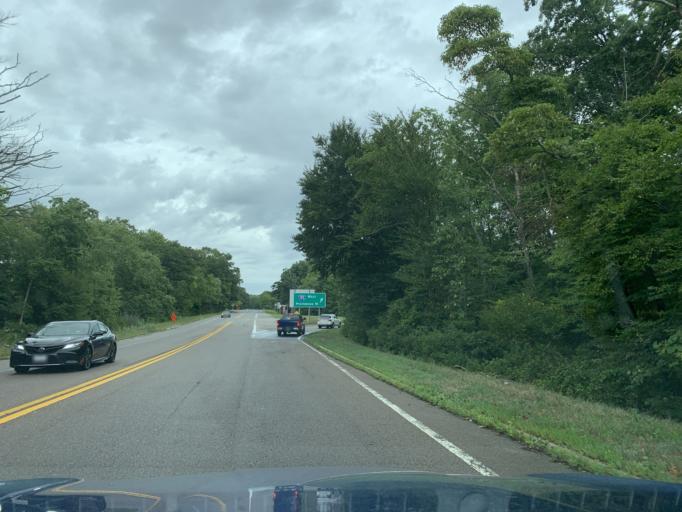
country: US
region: Rhode Island
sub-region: Bristol County
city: Warren
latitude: 41.7753
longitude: -71.2612
